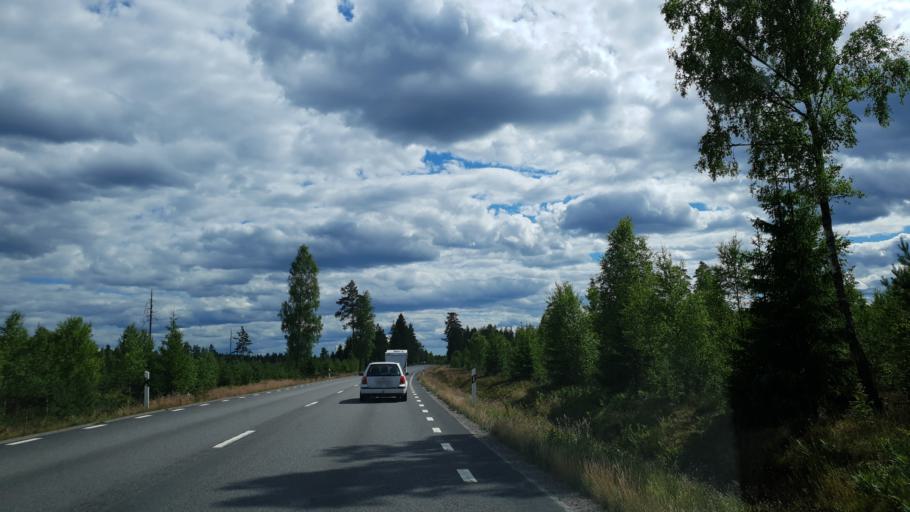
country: SE
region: Kronoberg
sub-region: Lessebo Kommun
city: Lessebo
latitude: 56.8046
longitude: 15.4124
